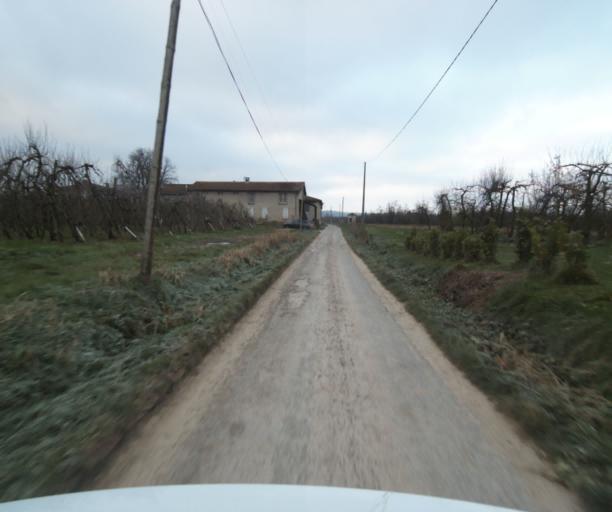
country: FR
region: Midi-Pyrenees
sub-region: Departement du Tarn-et-Garonne
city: Moissac
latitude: 44.0976
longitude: 1.1250
